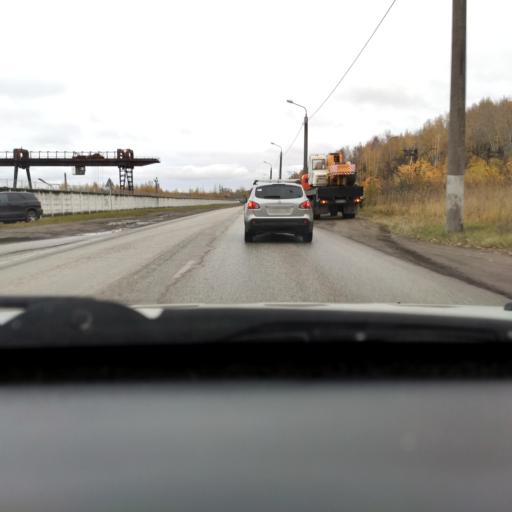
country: RU
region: Perm
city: Perm
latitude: 58.0949
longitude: 56.3555
